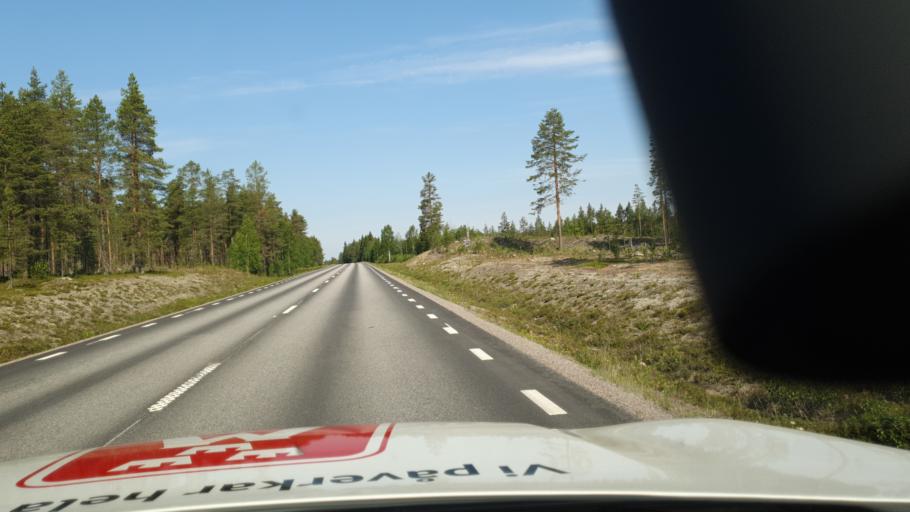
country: SE
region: Vaesterbotten
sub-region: Skelleftea Kommun
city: Langsele
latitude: 65.0422
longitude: 20.0803
